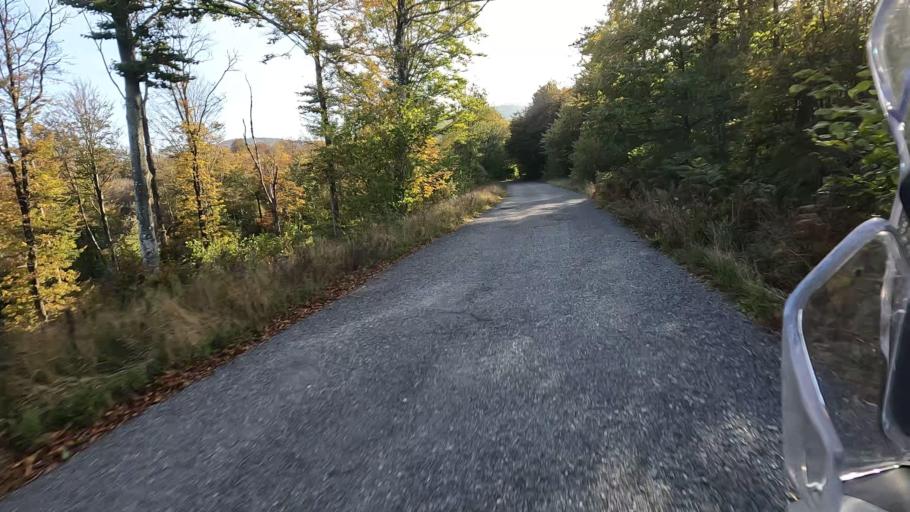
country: IT
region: Liguria
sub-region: Provincia di Savona
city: Urbe
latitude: 44.4476
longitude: 8.5796
